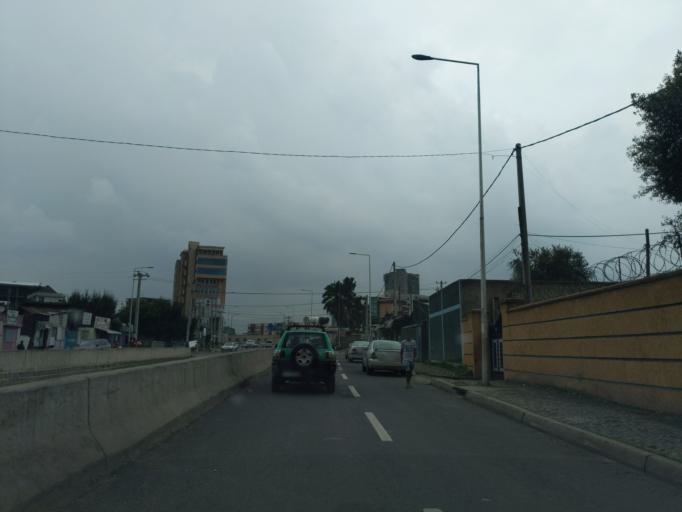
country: ET
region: Adis Abeba
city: Addis Ababa
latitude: 8.9853
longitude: 38.7654
